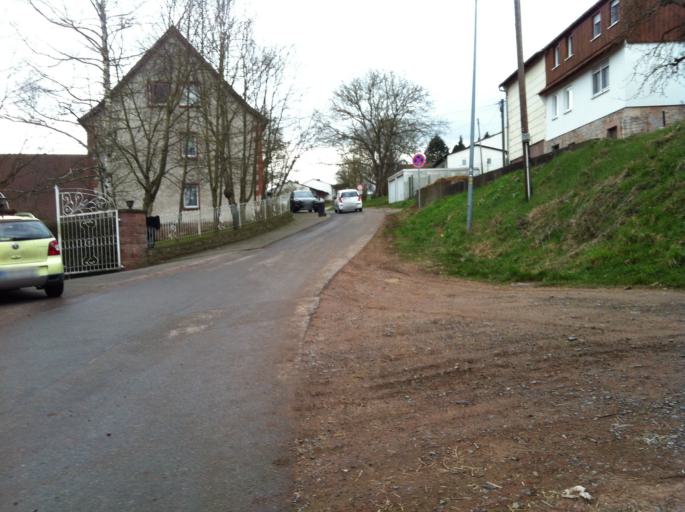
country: DE
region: Hesse
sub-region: Regierungsbezirk Darmstadt
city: Erbach
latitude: 49.6671
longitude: 8.9501
